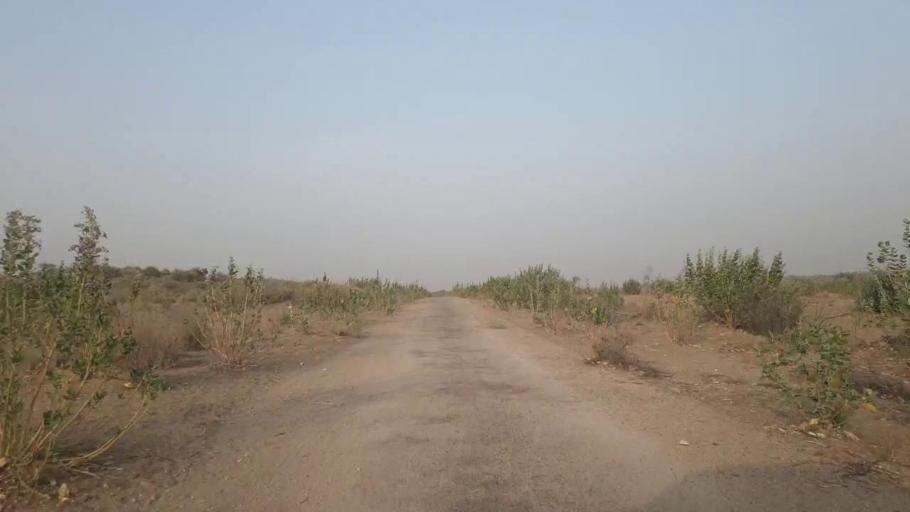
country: PK
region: Sindh
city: Chor
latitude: 25.5023
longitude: 69.9328
